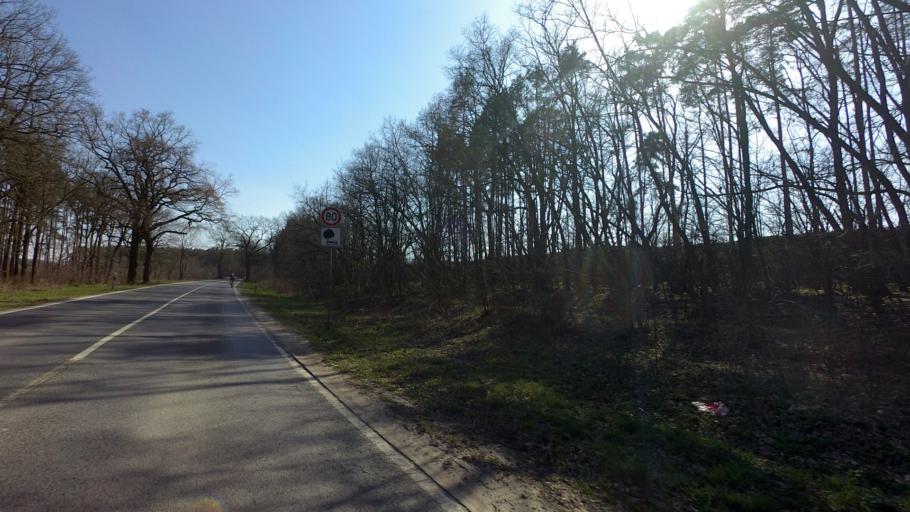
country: DE
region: Brandenburg
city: Leegebruch
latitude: 52.7355
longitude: 13.1796
